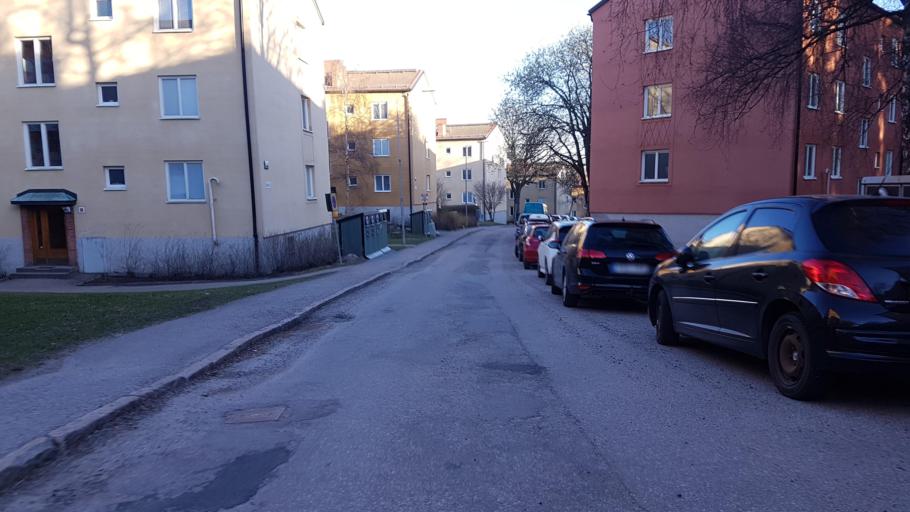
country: SE
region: Stockholm
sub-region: Stockholms Kommun
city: Arsta
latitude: 59.2634
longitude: 18.0752
